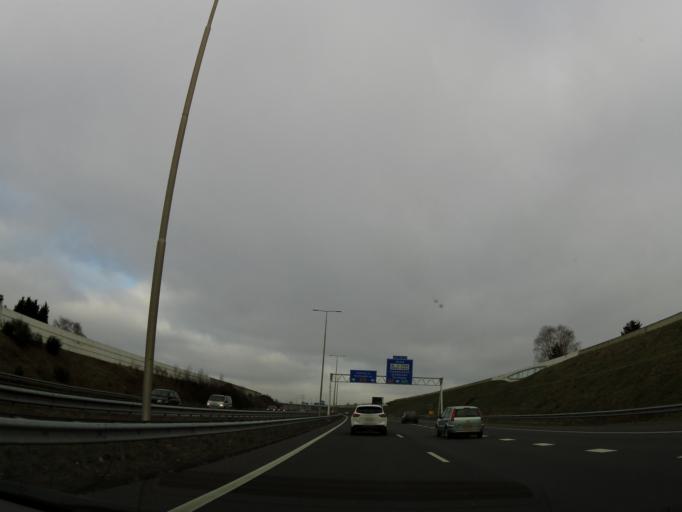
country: NL
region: Limburg
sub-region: Gemeente Venlo
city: Tegelen
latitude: 51.3720
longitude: 6.1231
